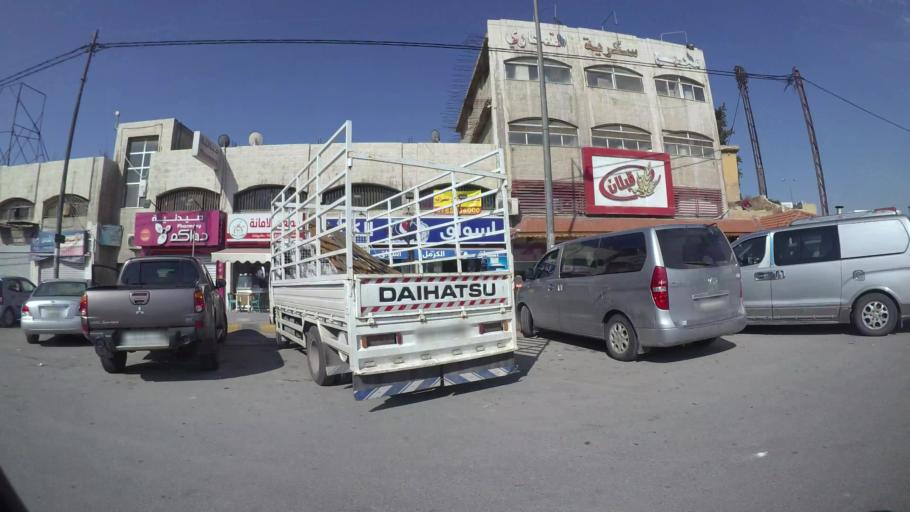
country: JO
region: Amman
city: Al Bunayyat ash Shamaliyah
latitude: 31.9166
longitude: 35.9030
